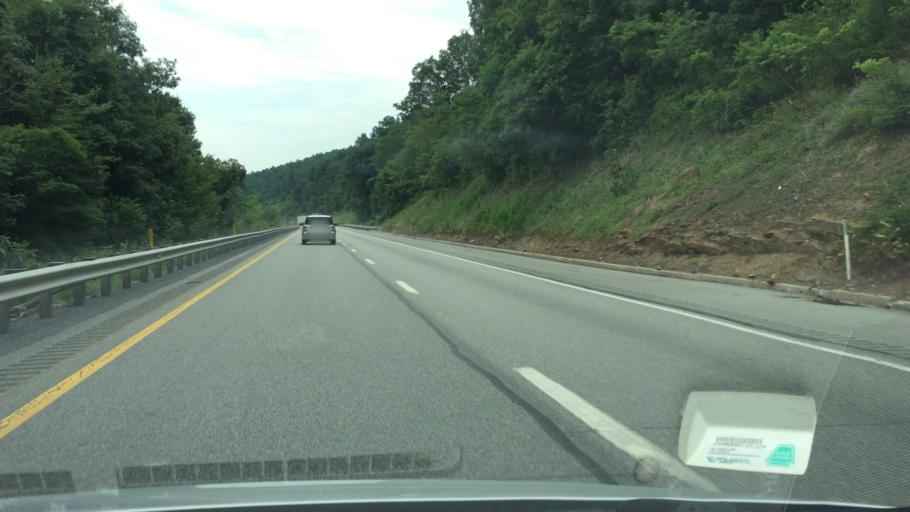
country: US
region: Pennsylvania
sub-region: Bedford County
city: Earlston
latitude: 39.8662
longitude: -78.2615
